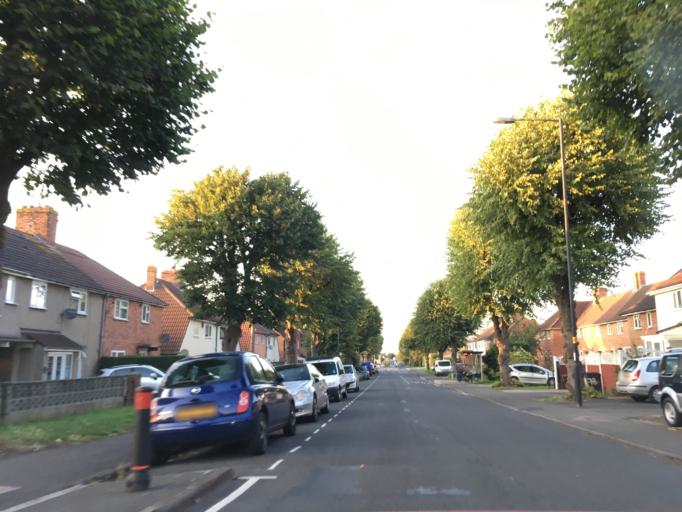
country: GB
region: England
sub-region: South Gloucestershire
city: Mangotsfield
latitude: 51.4758
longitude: -2.5182
